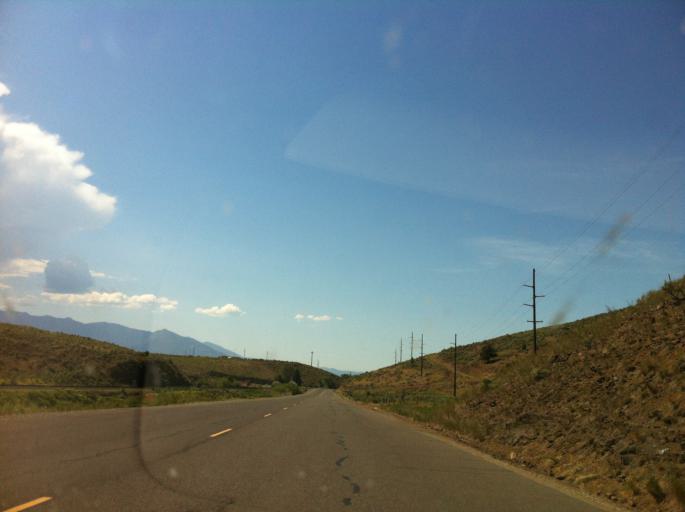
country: US
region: Oregon
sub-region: Baker County
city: Baker City
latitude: 44.7210
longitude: -117.7767
